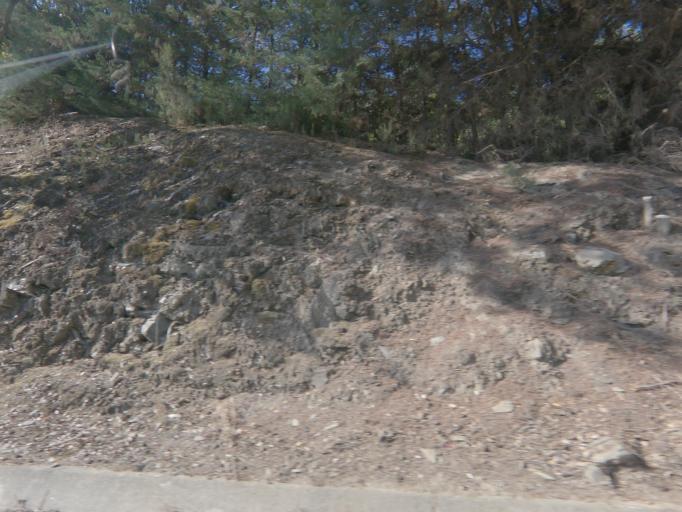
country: PT
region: Vila Real
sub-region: Sabrosa
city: Vilela
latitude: 41.1975
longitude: -7.5523
